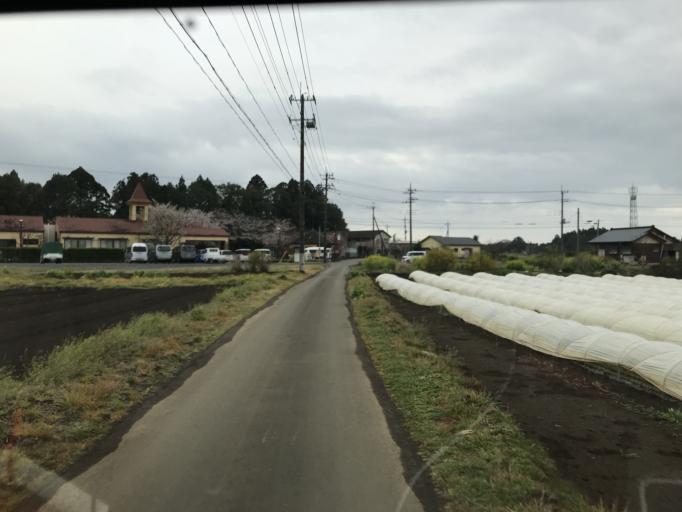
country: JP
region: Chiba
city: Sawara
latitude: 35.8567
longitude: 140.5149
